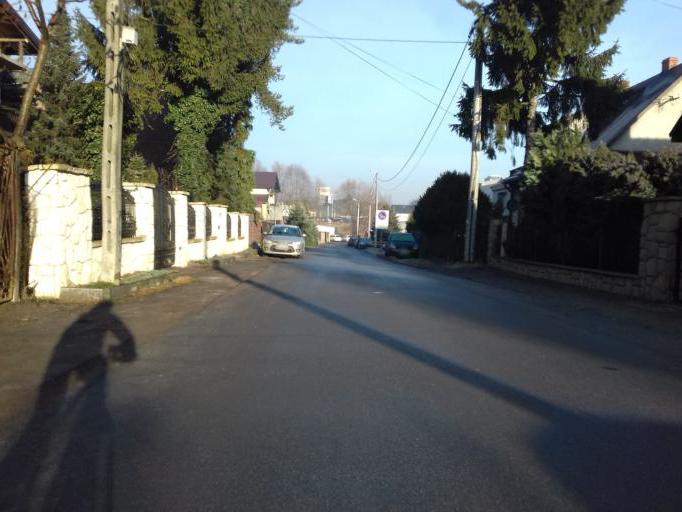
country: PL
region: Lesser Poland Voivodeship
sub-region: Krakow
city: Krakow
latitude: 50.0256
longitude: 19.9627
